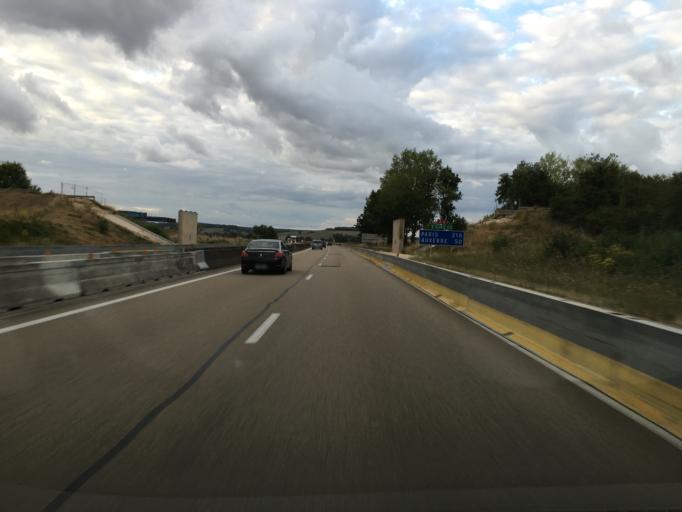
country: FR
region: Bourgogne
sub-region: Departement de l'Yonne
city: Avallon
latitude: 47.5234
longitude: 3.9874
